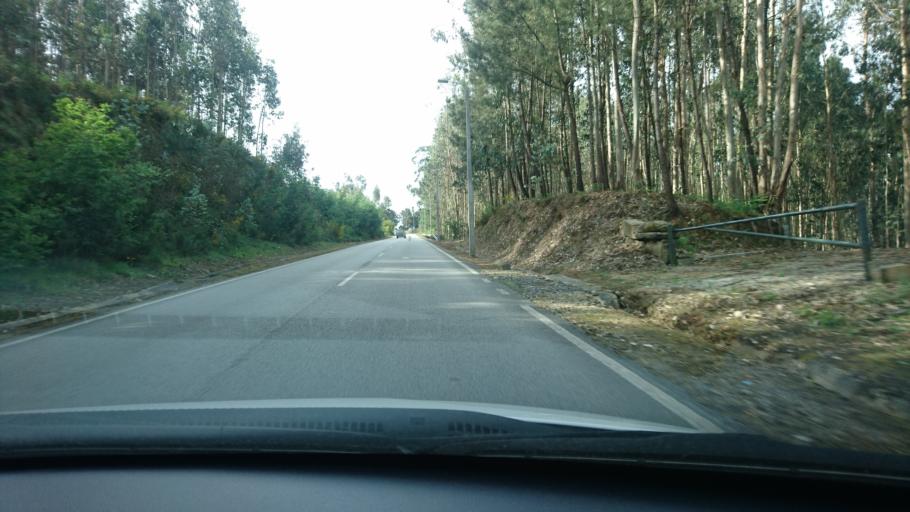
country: PT
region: Aveiro
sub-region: Oliveira de Azemeis
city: Sao Roque
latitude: 40.8661
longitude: -8.4760
